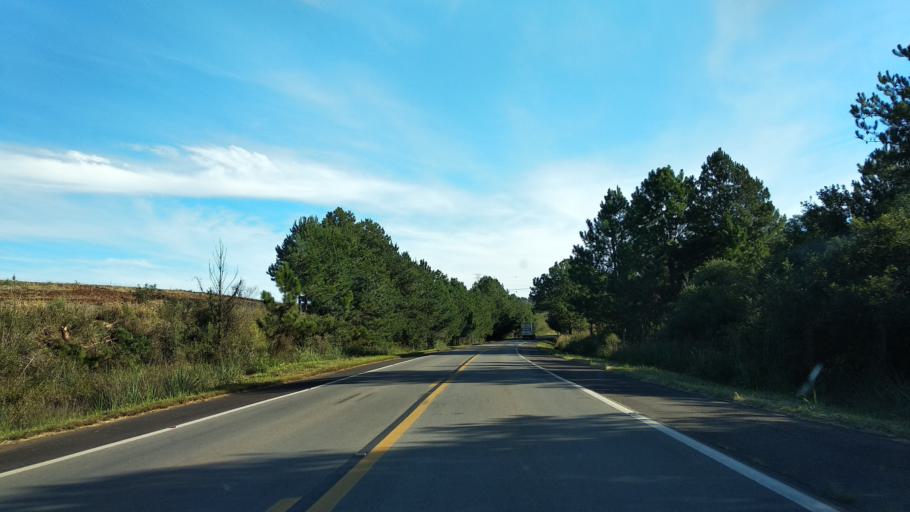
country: BR
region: Santa Catarina
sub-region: Celso Ramos
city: Celso Ramos
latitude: -27.5366
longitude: -51.4043
